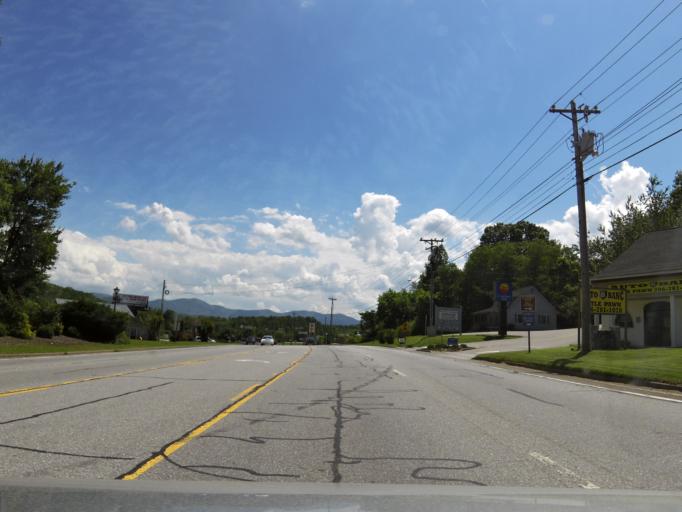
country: US
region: Georgia
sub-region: Union County
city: Blairsville
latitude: 34.8747
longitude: -83.9636
